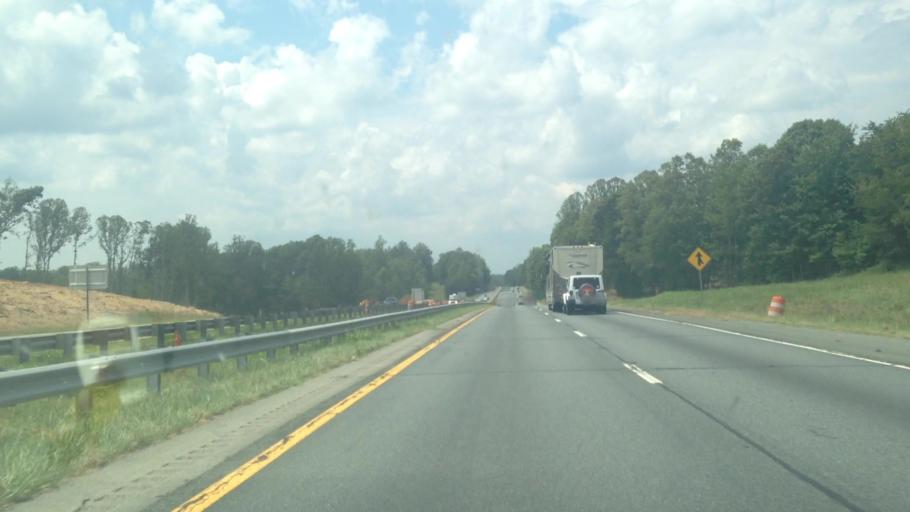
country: US
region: North Carolina
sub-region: Forsyth County
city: Rural Hall
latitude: 36.2114
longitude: -80.3039
